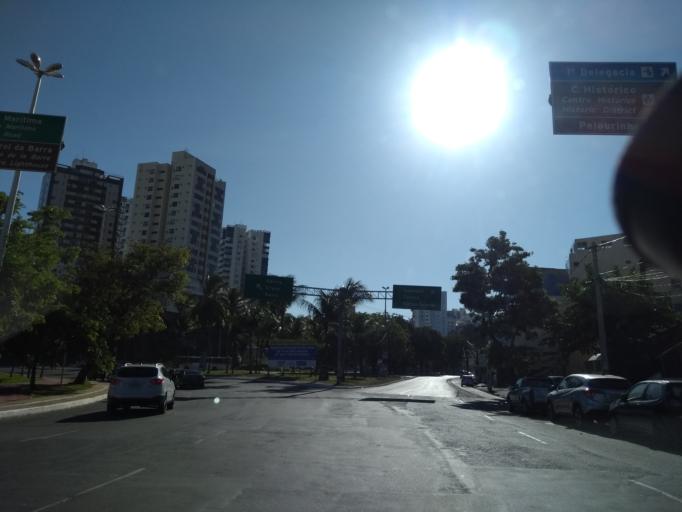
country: BR
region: Bahia
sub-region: Salvador
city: Salvador
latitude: -12.9879
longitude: -38.5123
